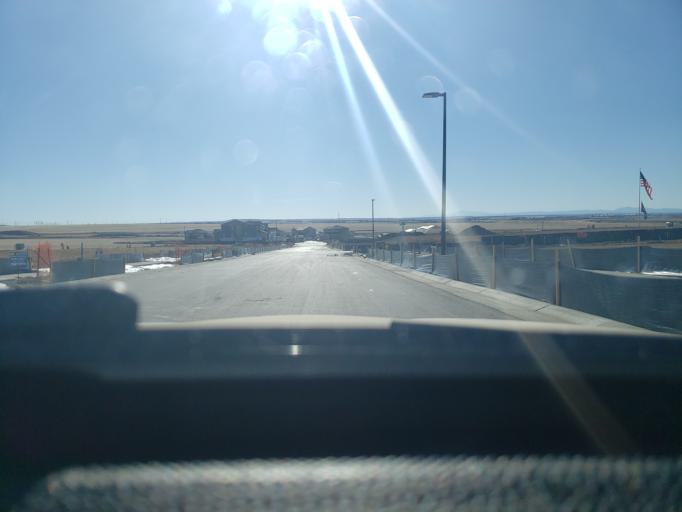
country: US
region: Colorado
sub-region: Adams County
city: Aurora
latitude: 39.7746
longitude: -104.7036
